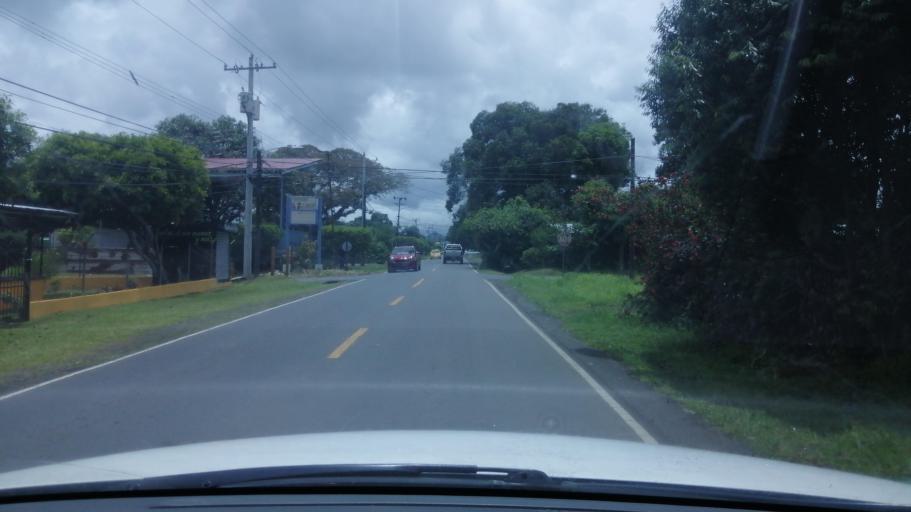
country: PA
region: Chiriqui
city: David
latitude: 8.4401
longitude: -82.4291
